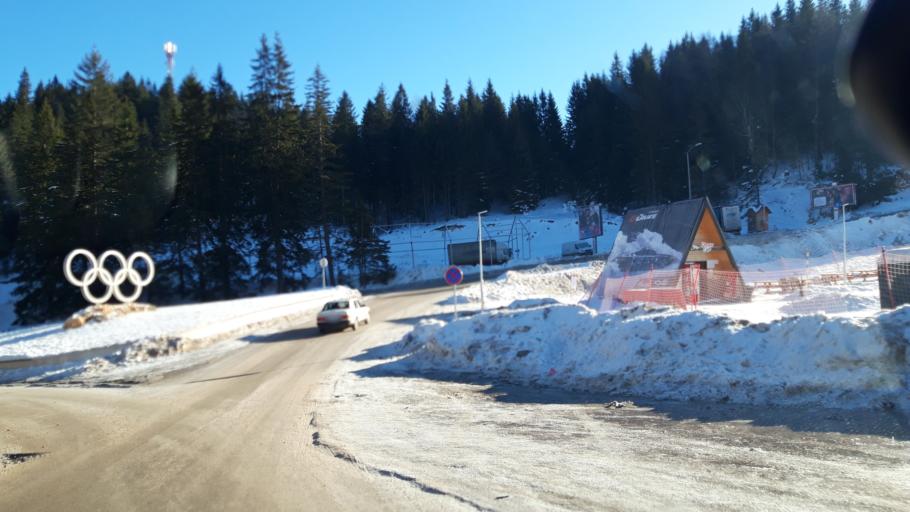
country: BA
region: Republika Srpska
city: Koran
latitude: 43.7373
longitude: 18.5666
